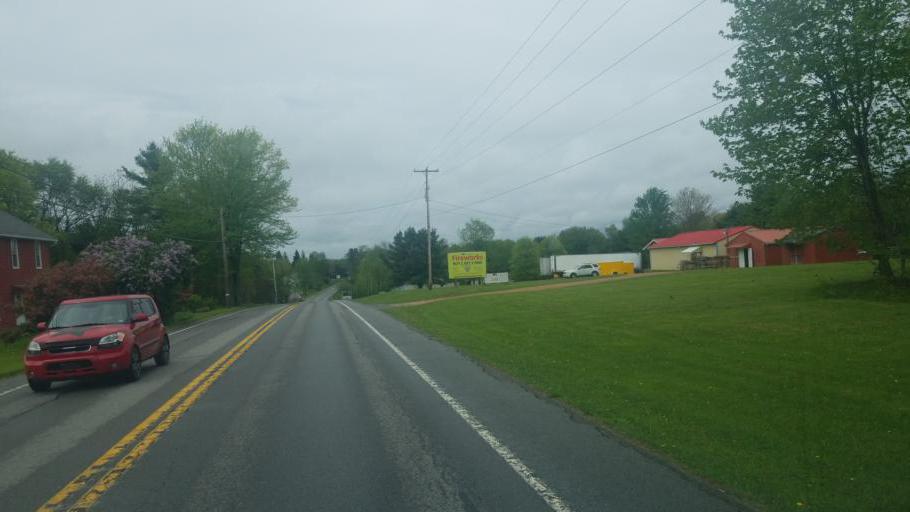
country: US
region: Pennsylvania
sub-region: Forest County
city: Marienville
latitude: 41.4451
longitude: -79.1761
